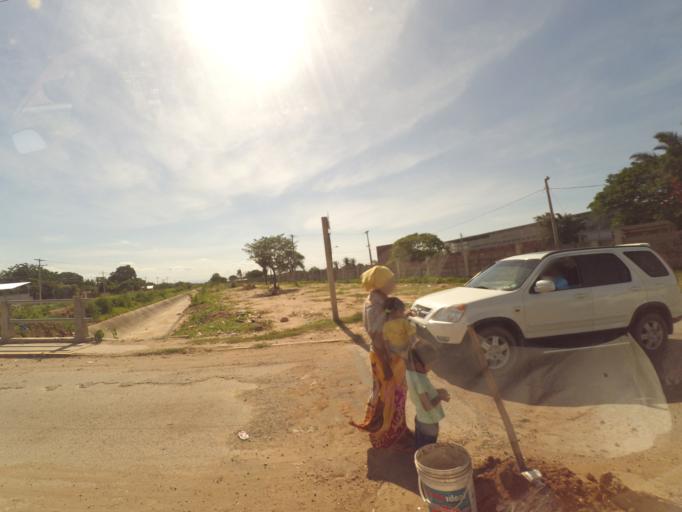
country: BO
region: Santa Cruz
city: Cotoca
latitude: -17.7765
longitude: -63.1078
